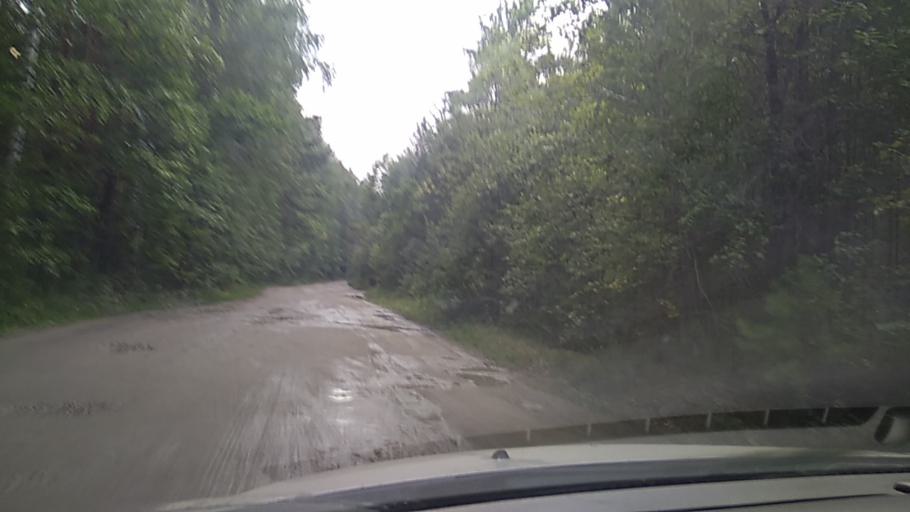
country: RU
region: Chelyabinsk
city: Kyshtym
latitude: 55.6777
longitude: 60.5869
